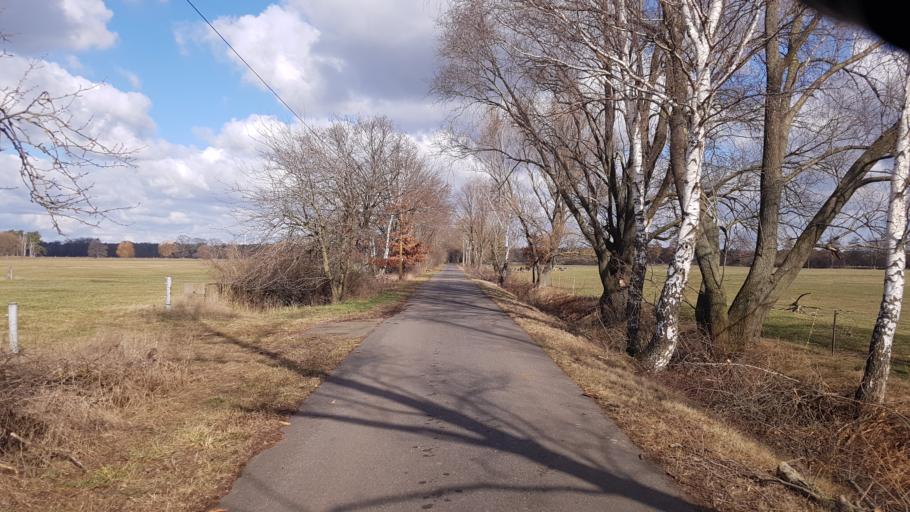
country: DE
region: Brandenburg
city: Falkenberg
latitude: 51.5962
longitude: 13.2170
